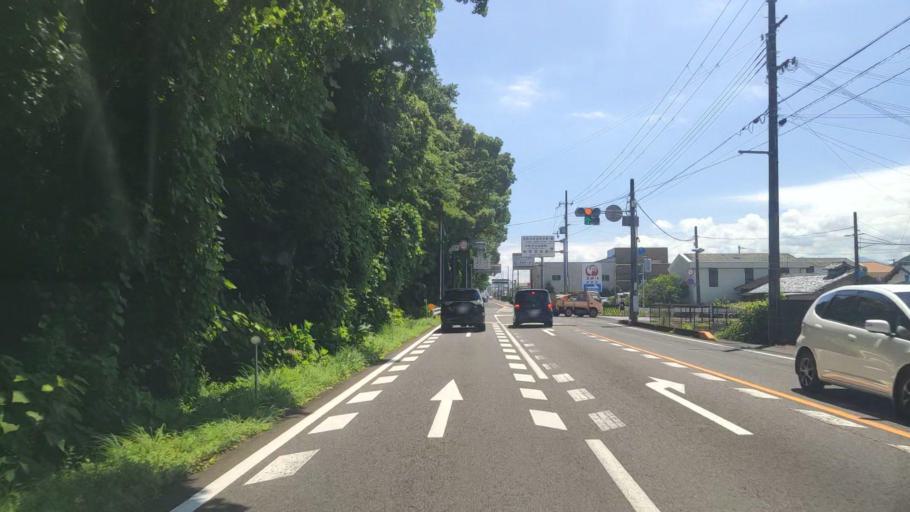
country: JP
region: Wakayama
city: Shingu
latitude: 33.8701
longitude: 136.0840
